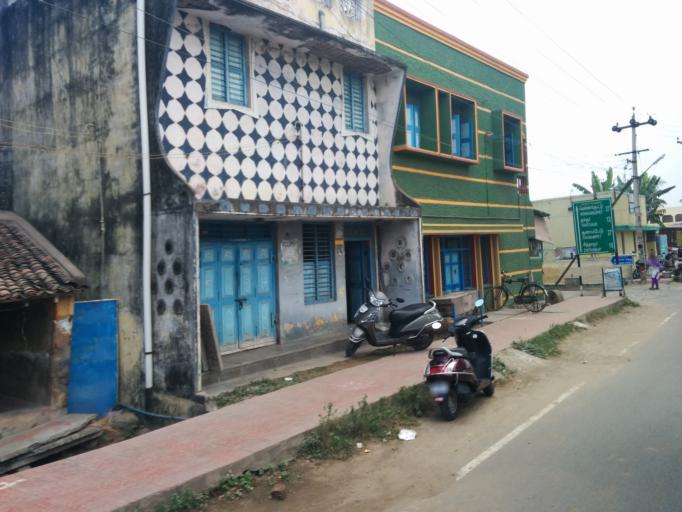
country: IN
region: Tamil Nadu
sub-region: Kancheepuram
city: Madurantakam
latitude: 12.5060
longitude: 79.8896
